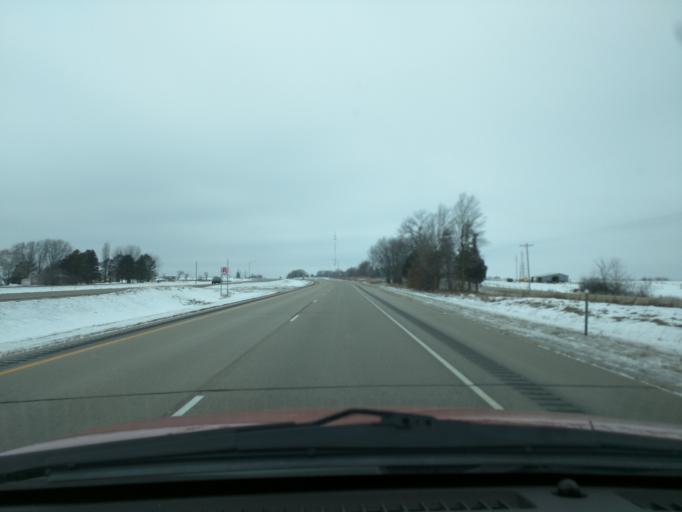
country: US
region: Wisconsin
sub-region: Trempealeau County
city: Trempealeau
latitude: 43.9117
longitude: -91.5456
